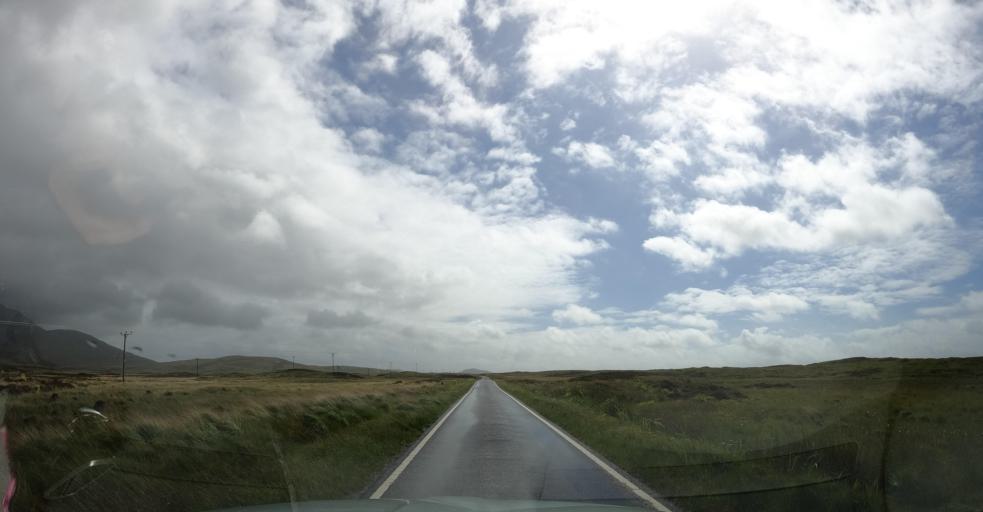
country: GB
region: Scotland
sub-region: Eilean Siar
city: Isle of South Uist
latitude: 57.2797
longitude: -7.3662
